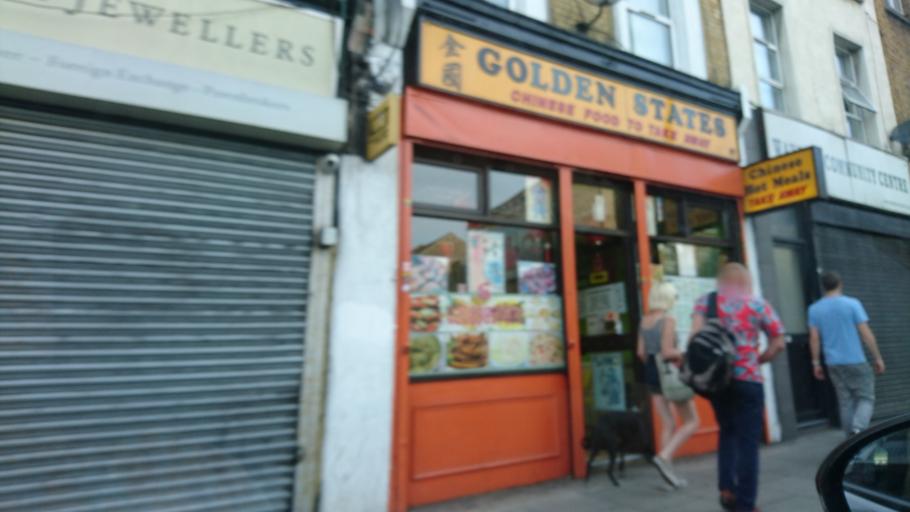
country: GB
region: England
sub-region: Greater London
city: Hackney
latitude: 51.5512
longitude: -0.0517
